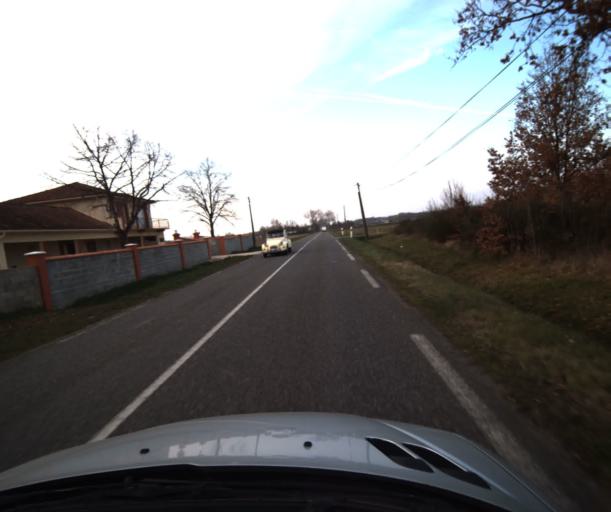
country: FR
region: Midi-Pyrenees
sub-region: Departement de la Haute-Garonne
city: Fronton
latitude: 43.8668
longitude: 1.3815
